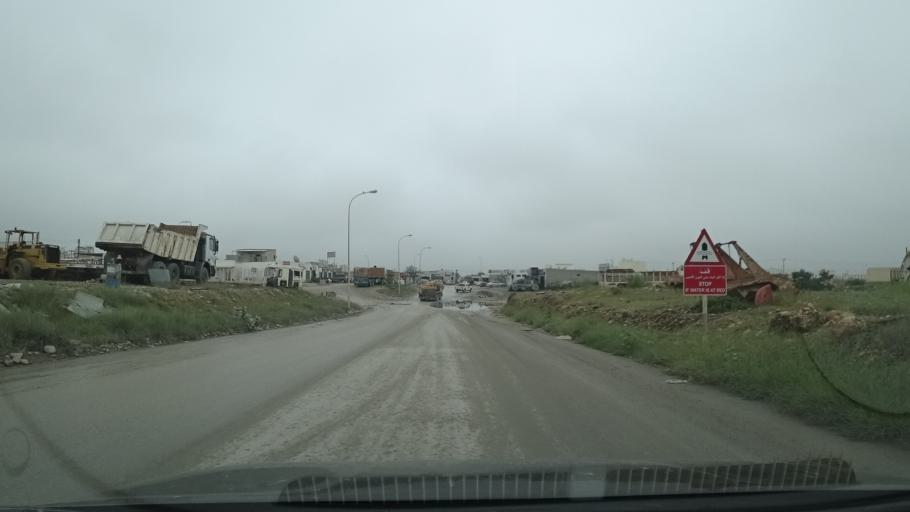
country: OM
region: Zufar
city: Salalah
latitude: 17.0288
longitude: 54.0444
